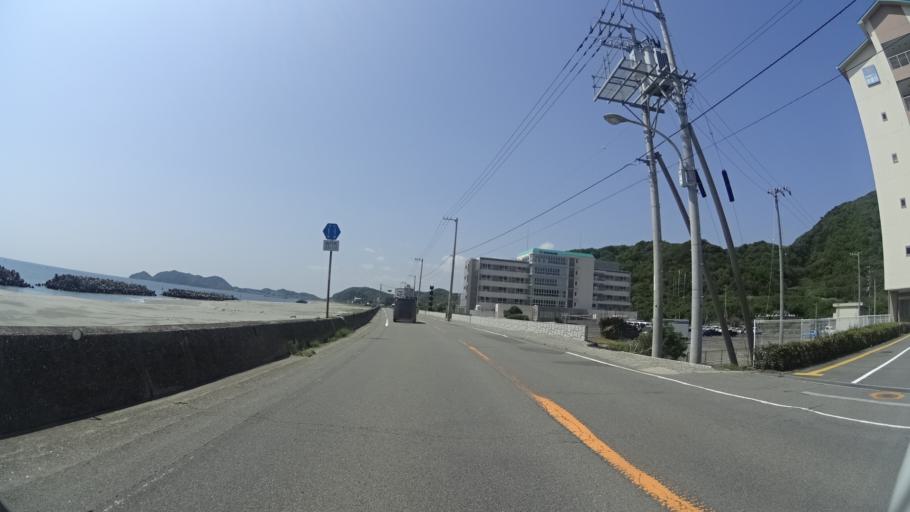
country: JP
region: Tokushima
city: Narutocho-mitsuishi
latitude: 34.2066
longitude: 134.6266
